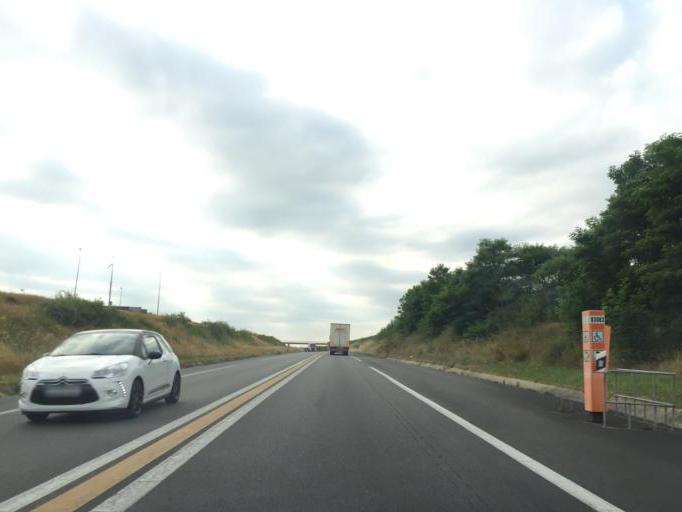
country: FR
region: Auvergne
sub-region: Departement de l'Allier
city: Diou
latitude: 46.5031
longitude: 3.7828
